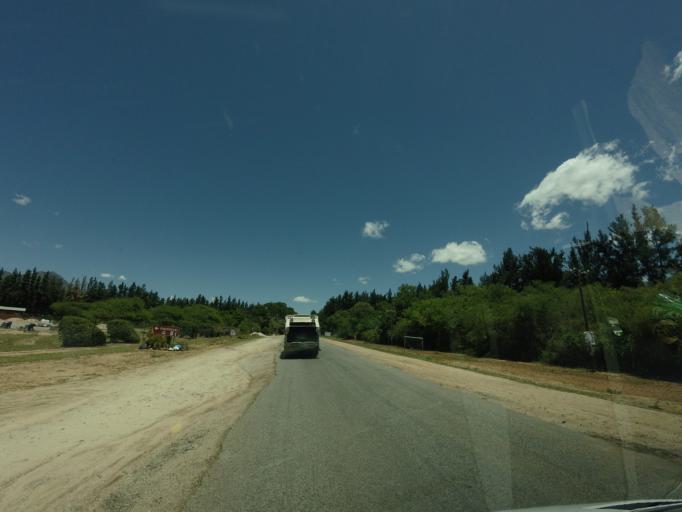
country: ZA
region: Limpopo
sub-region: Mopani District Municipality
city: Hoedspruit
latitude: -24.4041
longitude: 30.7813
